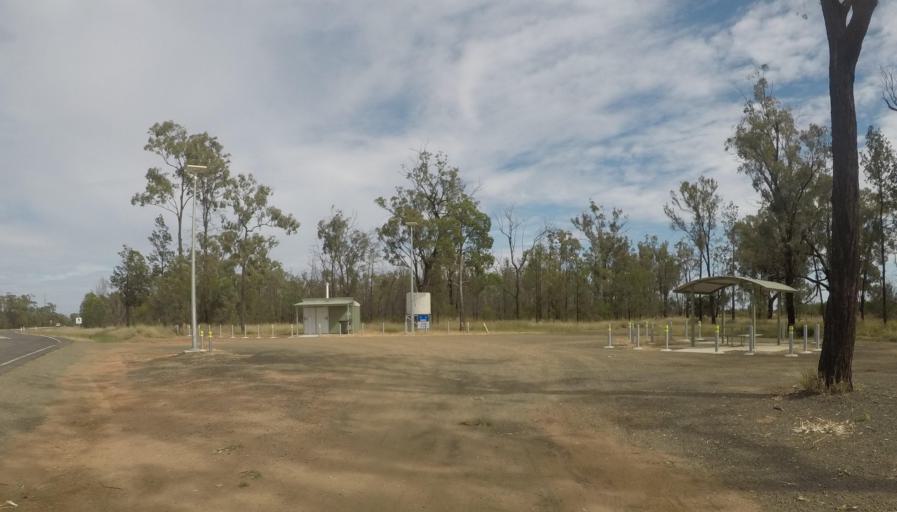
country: AU
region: Queensland
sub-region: Maranoa
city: Roma
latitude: -26.6210
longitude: 149.4572
